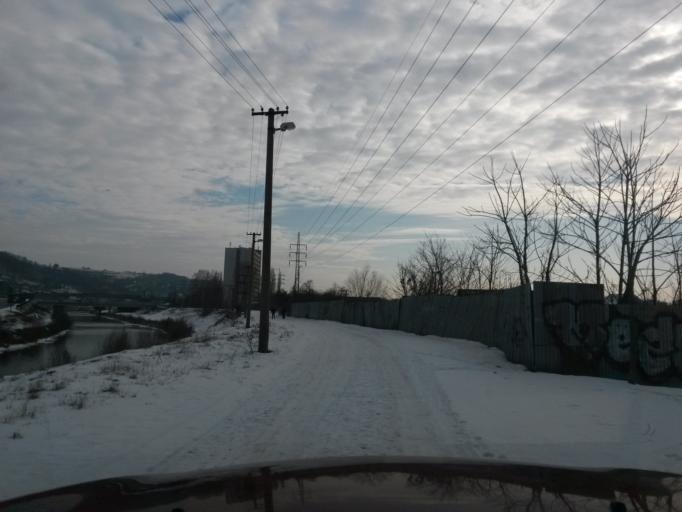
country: SK
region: Kosicky
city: Kosice
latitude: 48.7255
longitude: 21.2703
